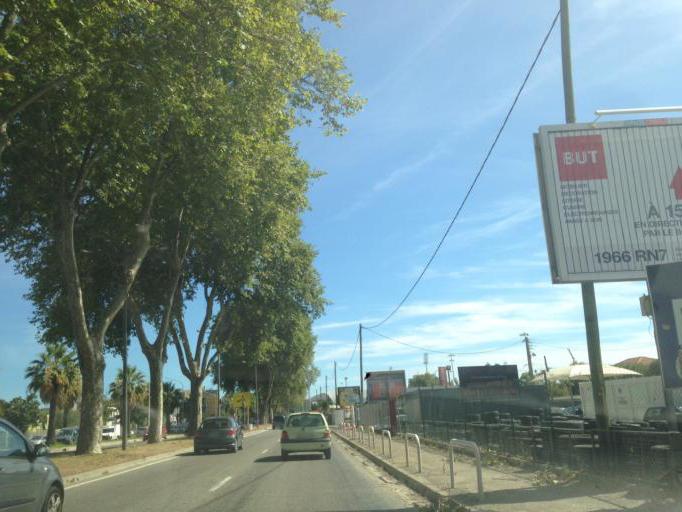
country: FR
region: Provence-Alpes-Cote d'Azur
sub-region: Departement des Alpes-Maritimes
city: Saint-Laurent-du-Var
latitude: 43.6843
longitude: 7.1981
